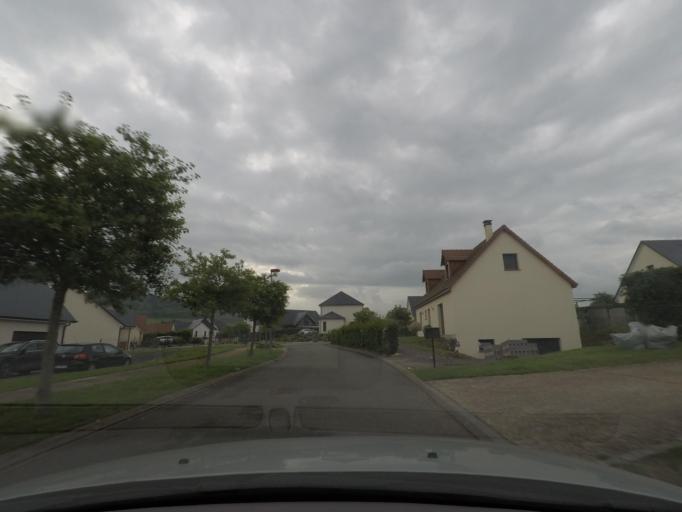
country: FR
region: Haute-Normandie
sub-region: Departement de la Seine-Maritime
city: Neufchatel-en-Bray
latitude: 49.7294
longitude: 1.4446
